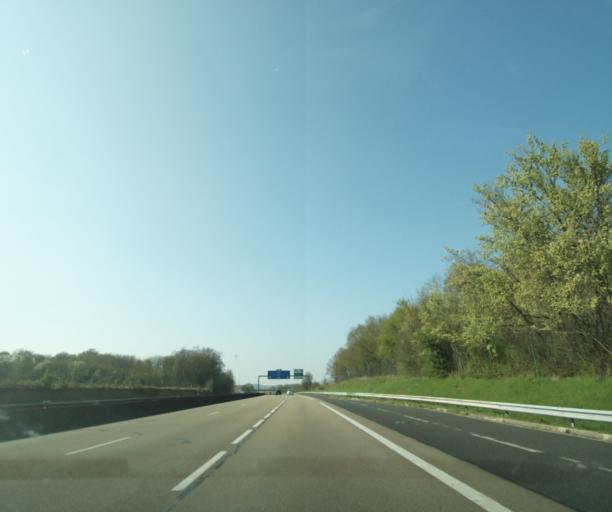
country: FR
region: Ile-de-France
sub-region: Departement de Seine-et-Marne
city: Cely
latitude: 48.4525
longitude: 2.5257
